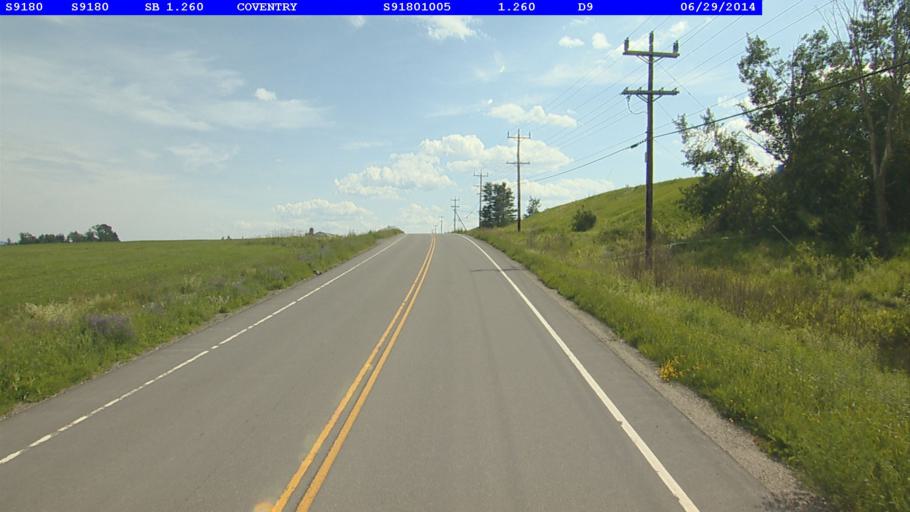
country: US
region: Vermont
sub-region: Orleans County
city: Newport
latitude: 44.9068
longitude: -72.2220
